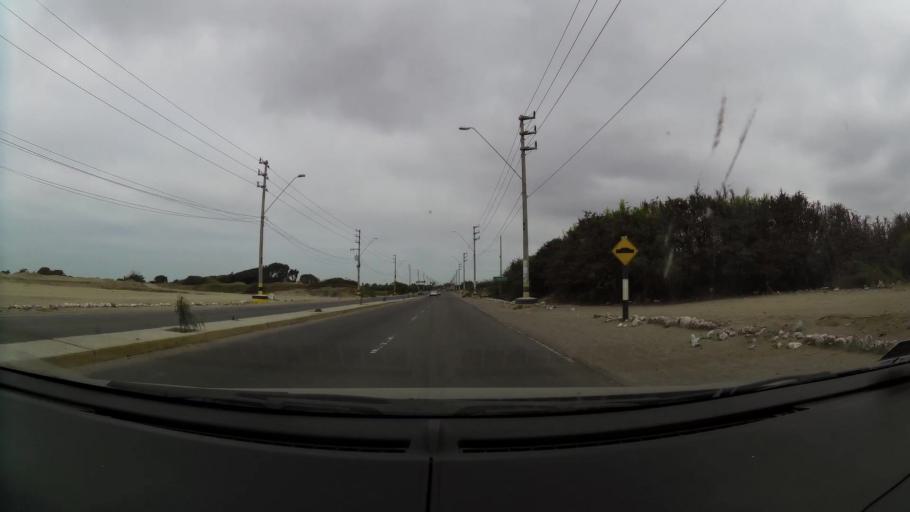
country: PE
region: La Libertad
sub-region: Provincia de Trujillo
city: La Esperanza
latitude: -8.0934
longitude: -79.0752
